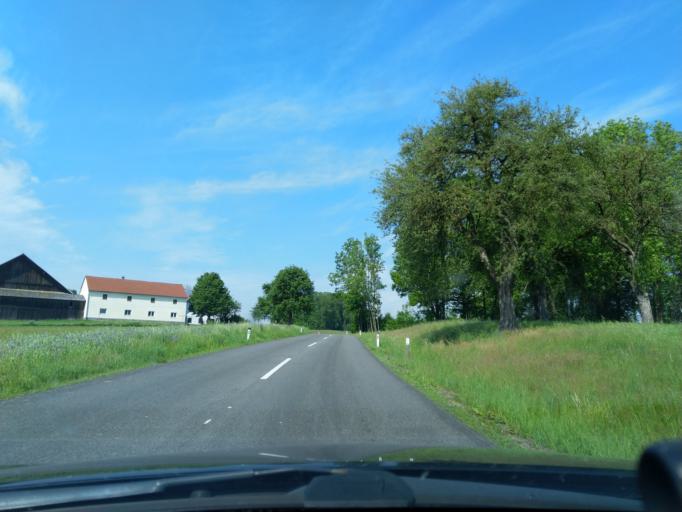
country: AT
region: Upper Austria
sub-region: Politischer Bezirk Scharding
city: Sankt Marienkirchen bei Schaerding
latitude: 48.3025
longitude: 13.4002
